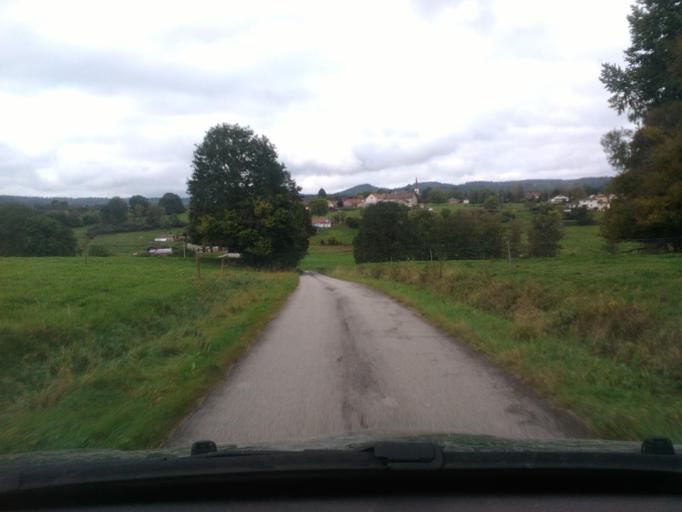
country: FR
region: Lorraine
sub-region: Departement des Vosges
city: Etival-Clairefontaine
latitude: 48.3481
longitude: 6.8395
